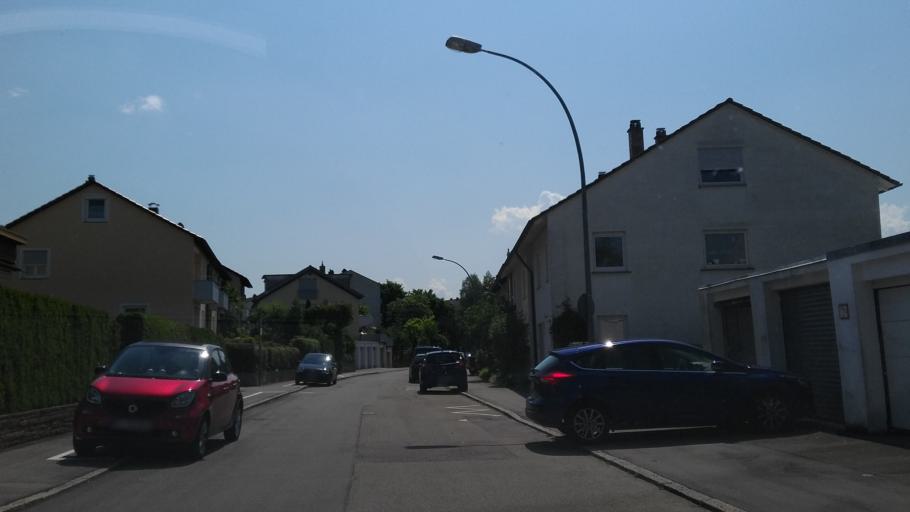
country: DE
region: Baden-Wuerttemberg
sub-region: Regierungsbezirk Stuttgart
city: Esslingen
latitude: 48.7364
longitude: 9.3364
